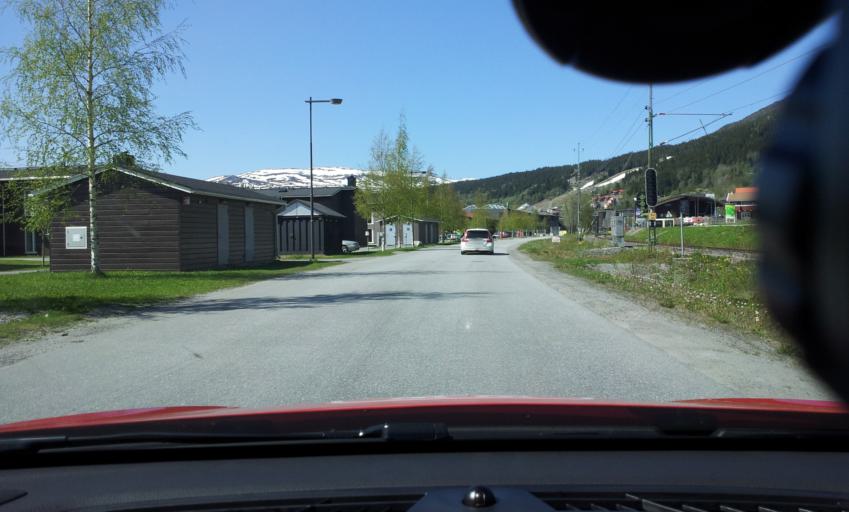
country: SE
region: Jaemtland
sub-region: Are Kommun
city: Are
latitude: 63.3964
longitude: 13.0810
